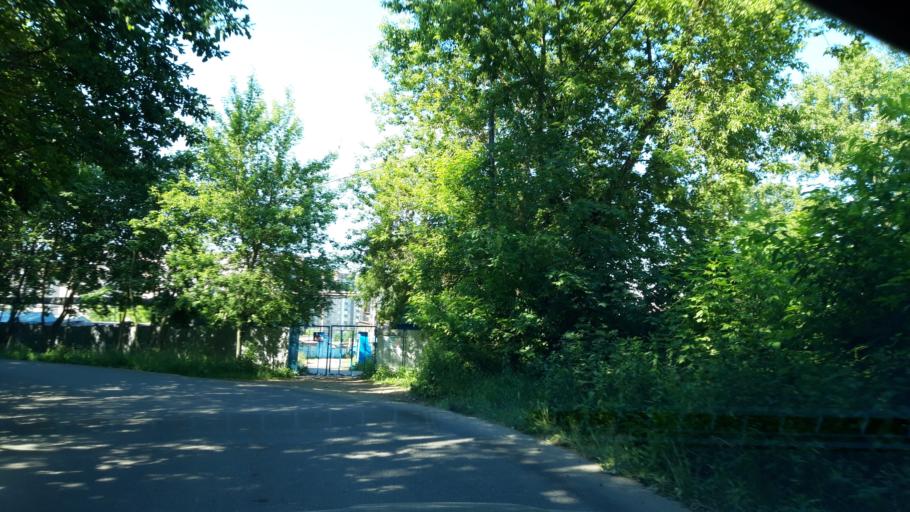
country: RU
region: Moscow
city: Zelenograd
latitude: 55.9853
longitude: 37.1705
